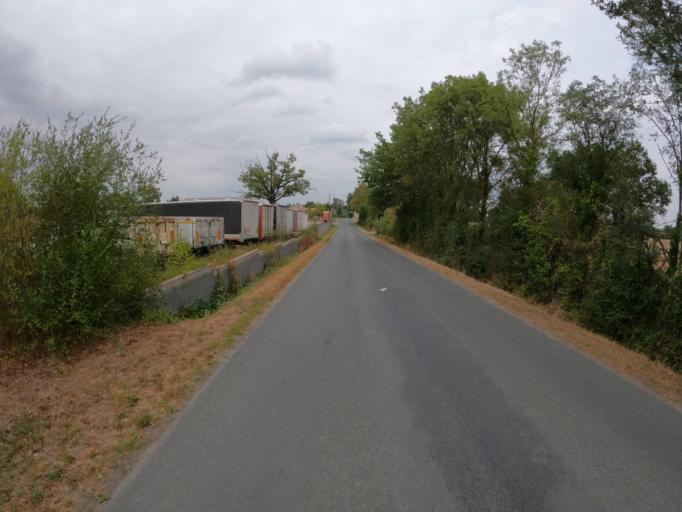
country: FR
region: Pays de la Loire
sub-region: Departement de la Vendee
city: Les Landes-Genusson
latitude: 46.9702
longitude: -1.1145
